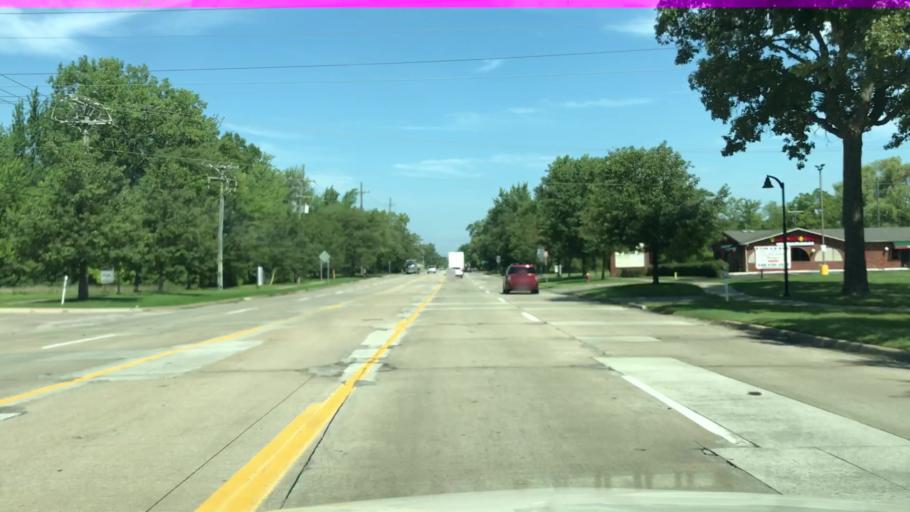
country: US
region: Michigan
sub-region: Wayne County
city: Wayne
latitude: 42.2489
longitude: -83.3477
